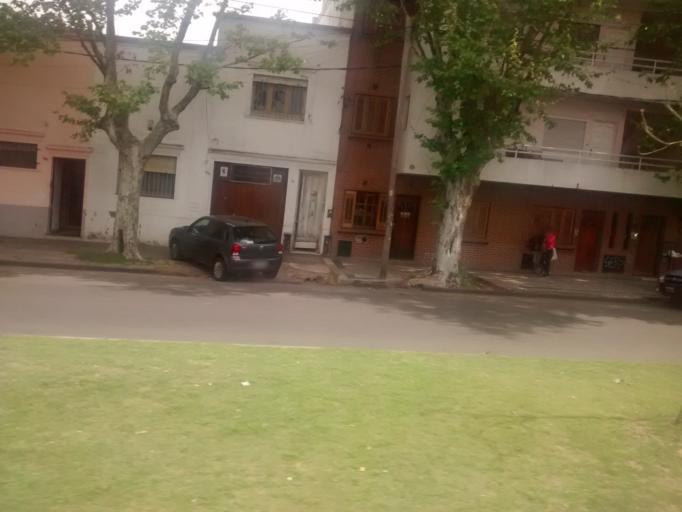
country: AR
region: Buenos Aires
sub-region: Partido de La Plata
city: La Plata
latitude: -34.9223
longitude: -57.9260
